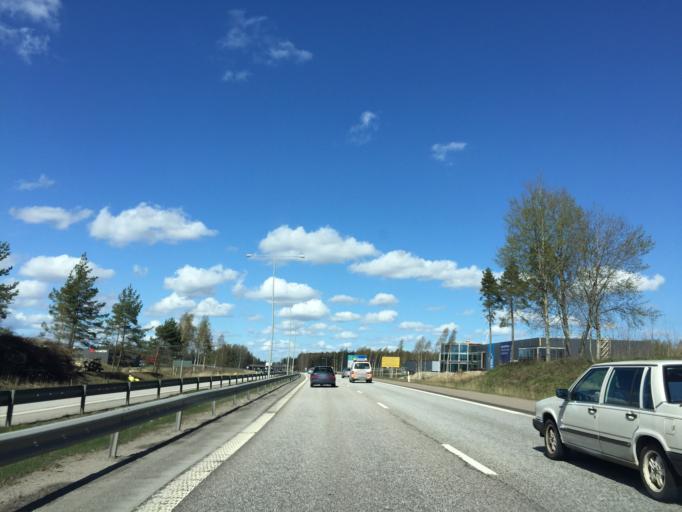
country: SE
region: OErebro
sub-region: Orebro Kommun
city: Orebro
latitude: 59.2336
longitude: 15.1441
